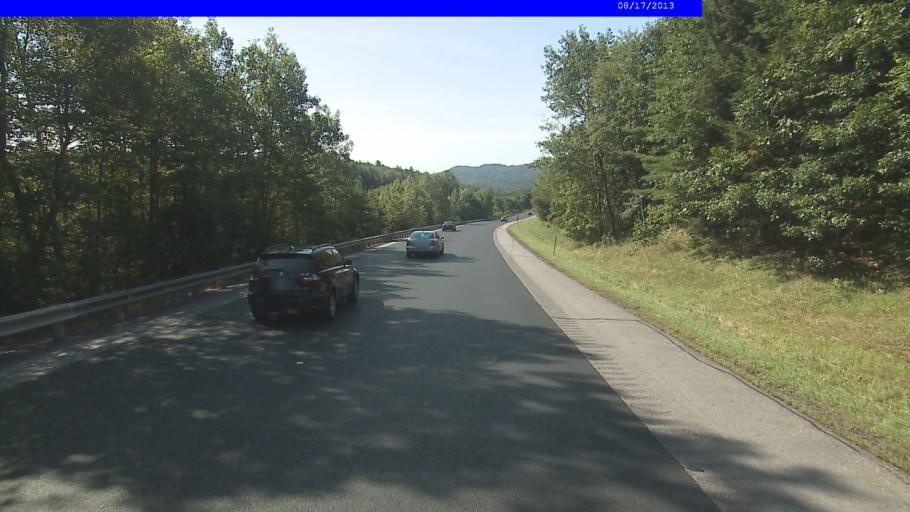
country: US
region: Vermont
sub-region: Windham County
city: Bellows Falls
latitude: 43.1451
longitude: -72.4749
